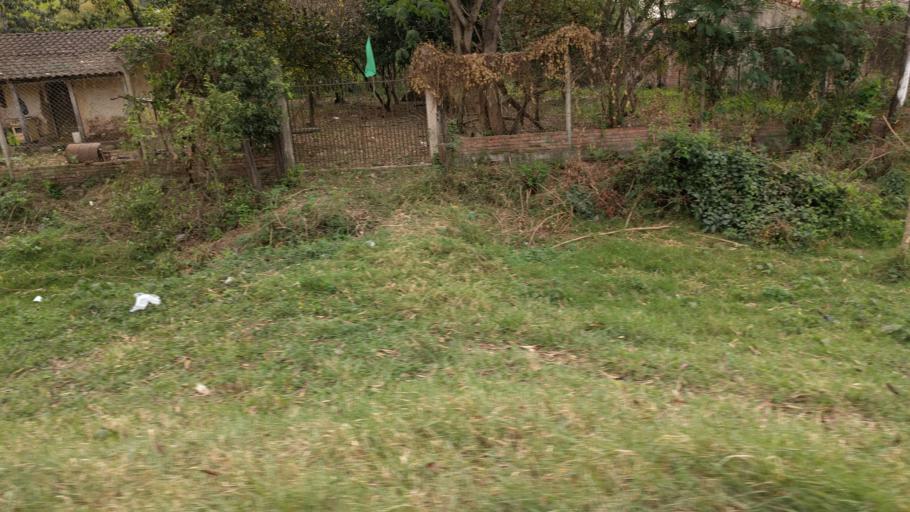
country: BO
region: Santa Cruz
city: Jorochito
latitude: -18.1476
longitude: -63.4856
